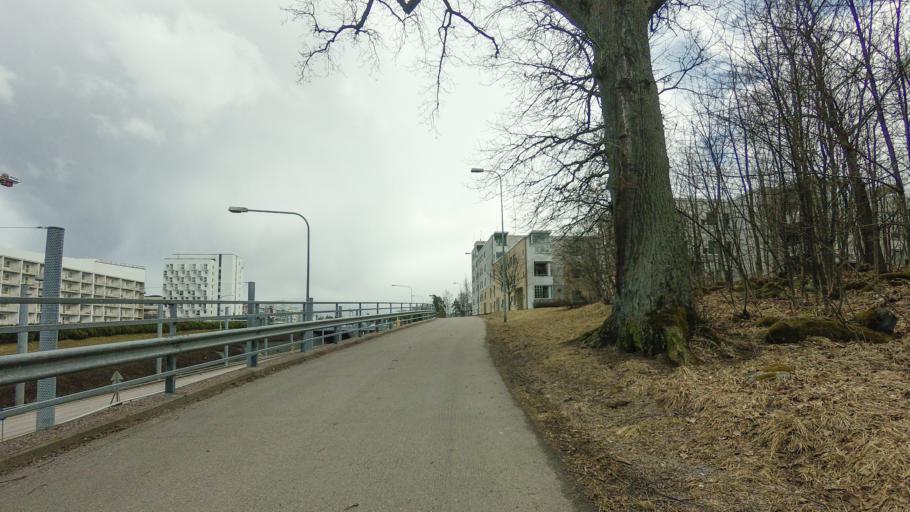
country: FI
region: Uusimaa
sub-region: Helsinki
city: Vantaa
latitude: 60.2056
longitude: 25.1165
